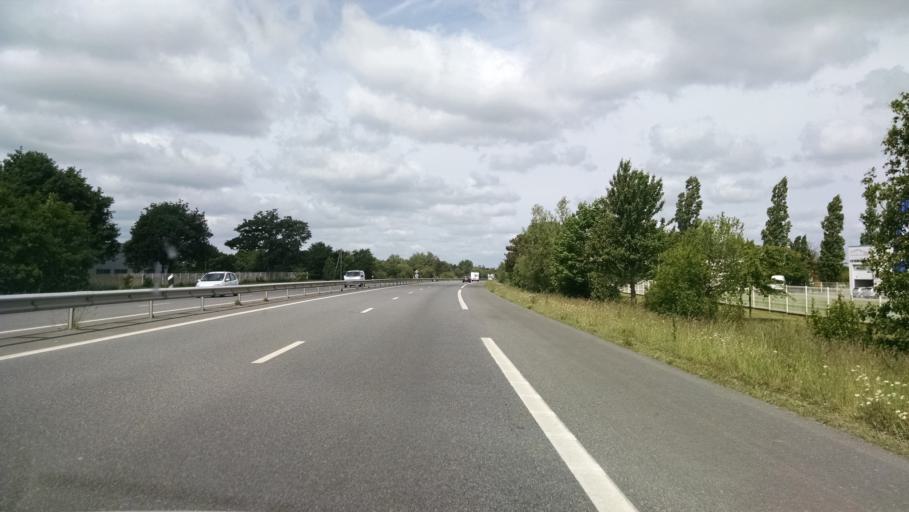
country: FR
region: Pays de la Loire
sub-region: Departement de la Loire-Atlantique
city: Besne
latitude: 47.4193
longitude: -2.0461
